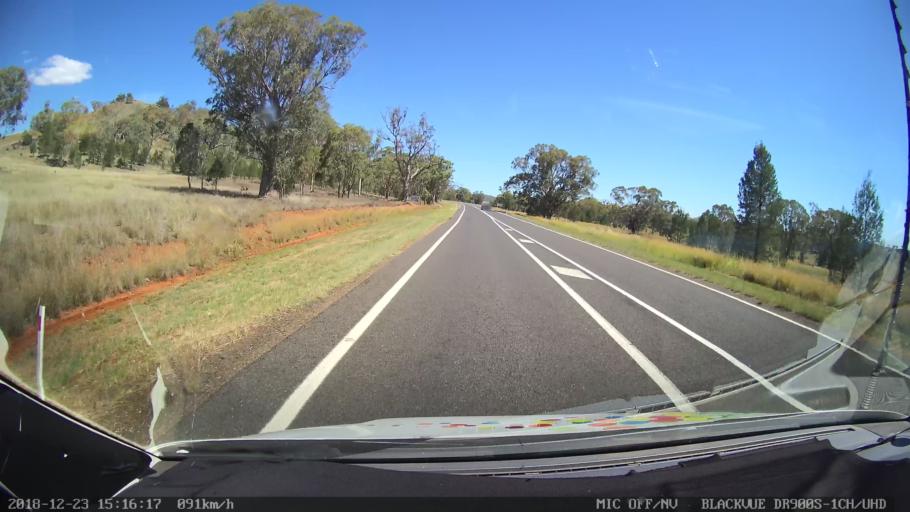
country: AU
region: New South Wales
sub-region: Tamworth Municipality
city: Manilla
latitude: -30.7968
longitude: 150.7476
